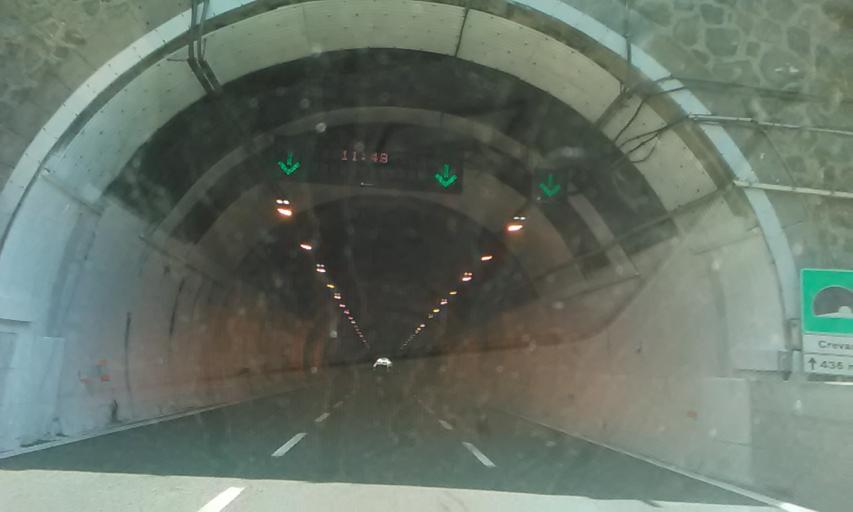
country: IT
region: Liguria
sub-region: Provincia di Genova
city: Mele
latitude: 44.4228
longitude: 8.7316
